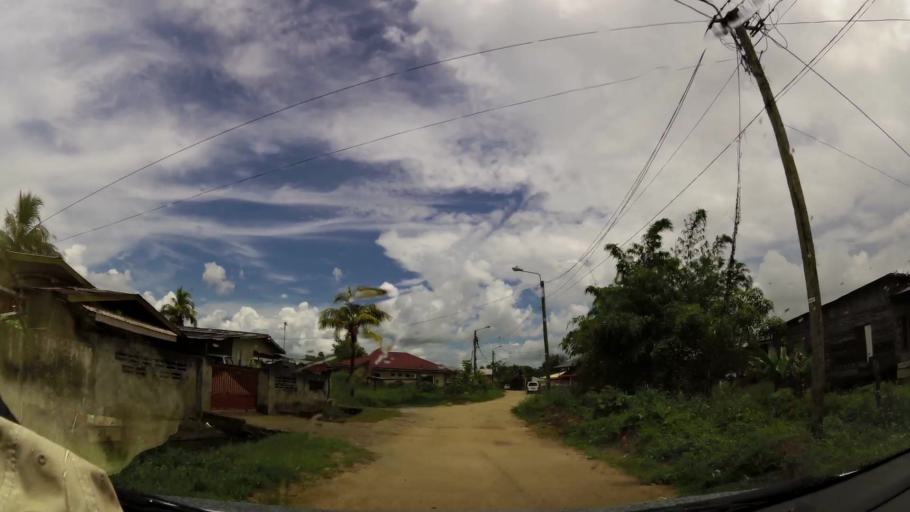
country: SR
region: Wanica
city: Lelydorp
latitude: 5.7903
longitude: -55.2198
